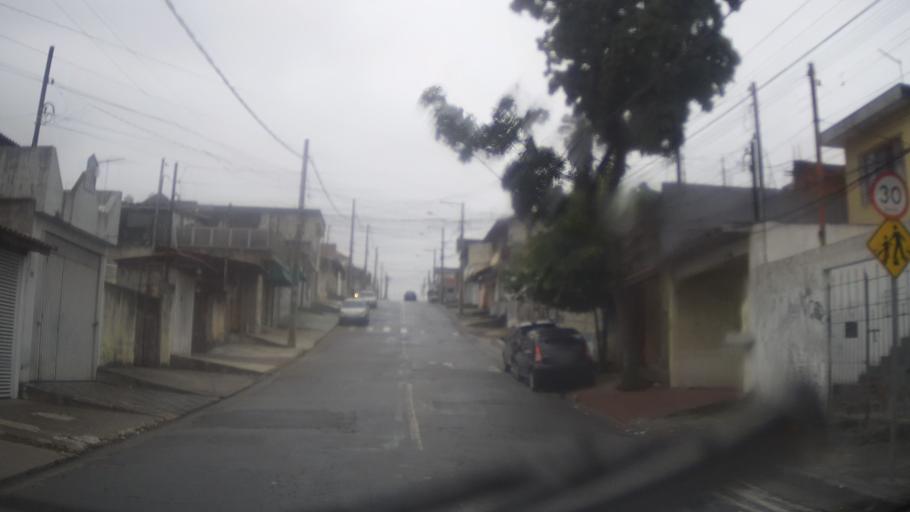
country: BR
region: Sao Paulo
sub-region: Guarulhos
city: Guarulhos
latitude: -23.4387
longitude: -46.5155
